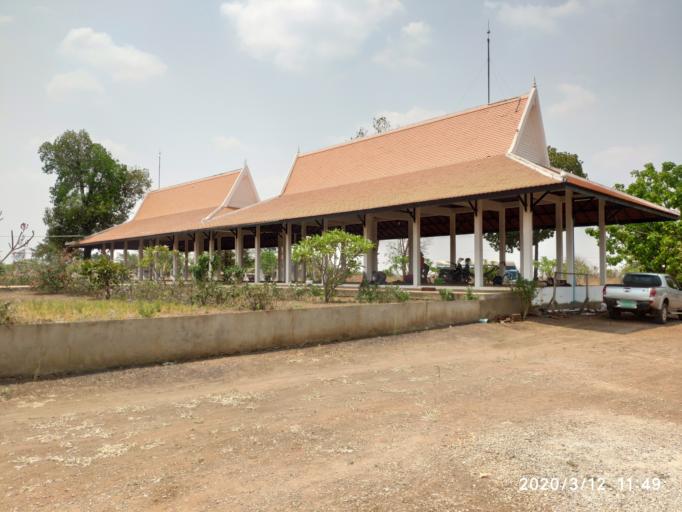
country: KH
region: Preah Vihear
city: Tbeng Meanchey
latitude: 13.7170
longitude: 104.5454
